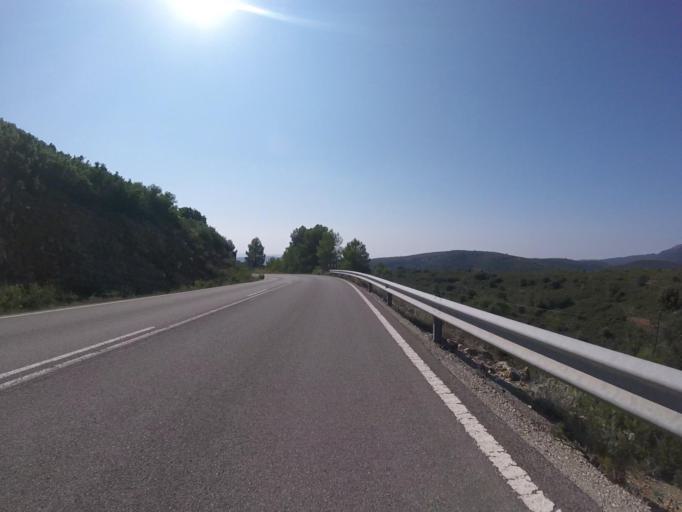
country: ES
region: Valencia
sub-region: Provincia de Castello
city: Benafigos
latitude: 40.2569
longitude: -0.2164
